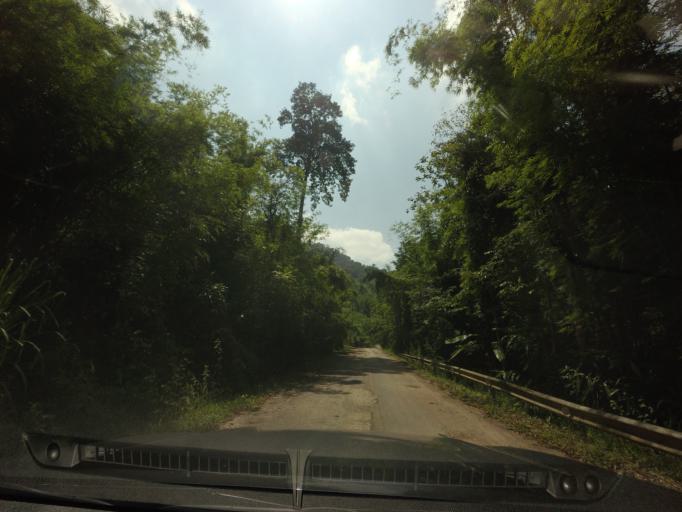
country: TH
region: Loei
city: Na Haeo
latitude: 17.5297
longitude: 100.9375
